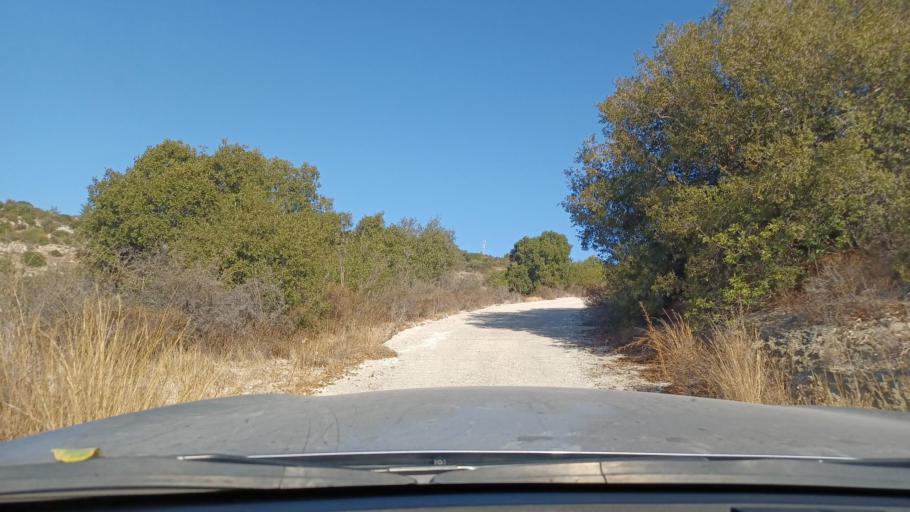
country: CY
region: Pafos
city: Polis
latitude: 35.0021
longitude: 32.4913
